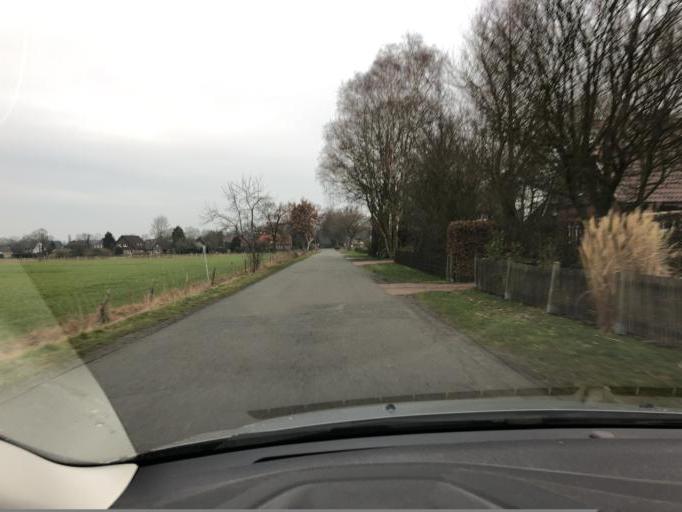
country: DE
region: Lower Saxony
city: Bad Zwischenahn
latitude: 53.1742
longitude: 8.0283
